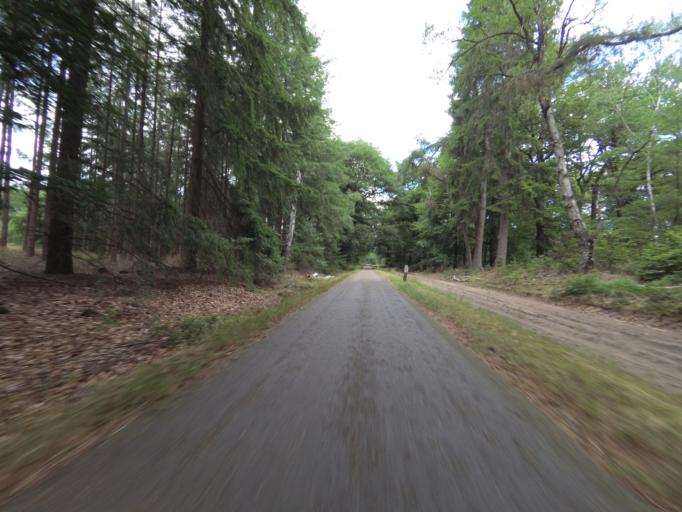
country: NL
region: Overijssel
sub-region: Gemeente Hof van Twente
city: Markelo
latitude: 52.3250
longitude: 6.4480
